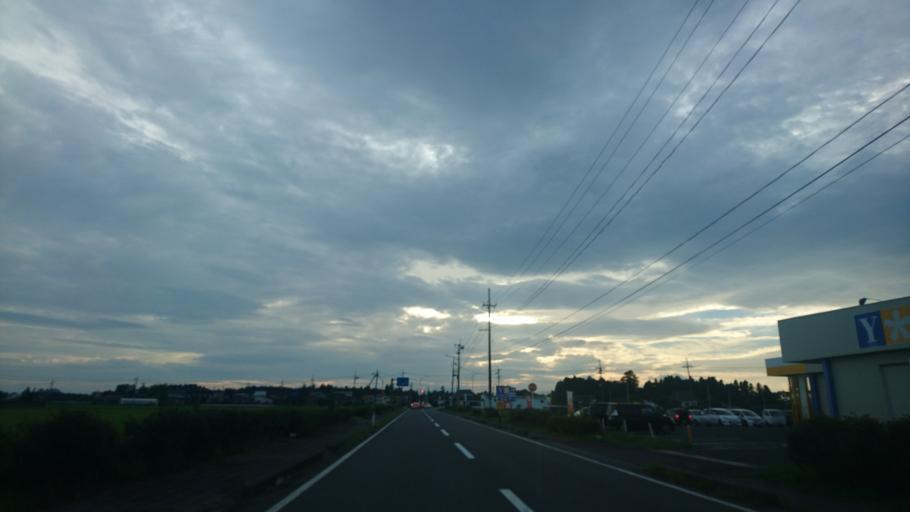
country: JP
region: Iwate
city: Ichinoseki
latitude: 38.7478
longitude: 141.0543
